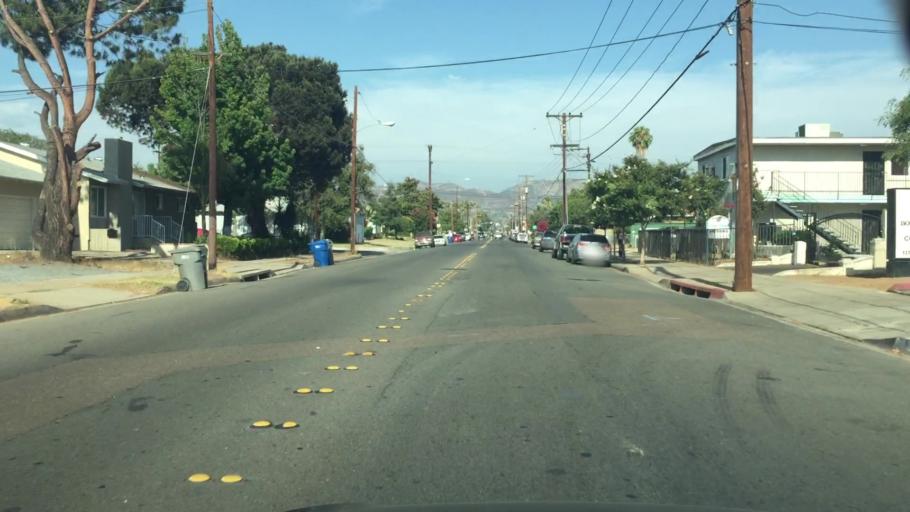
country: US
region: California
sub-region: San Diego County
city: Bostonia
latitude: 32.8002
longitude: -116.9414
